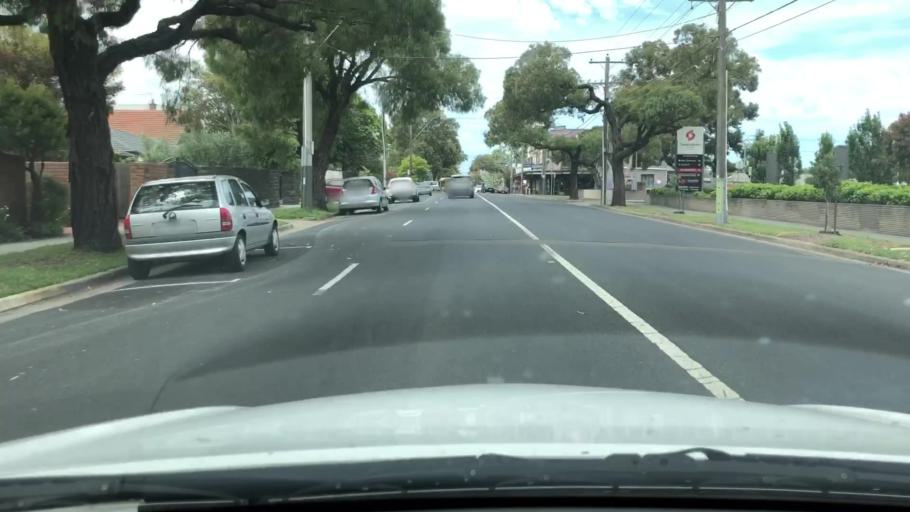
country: AU
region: Victoria
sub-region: Bayside
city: Black Rock
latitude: -37.9609
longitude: 145.0192
